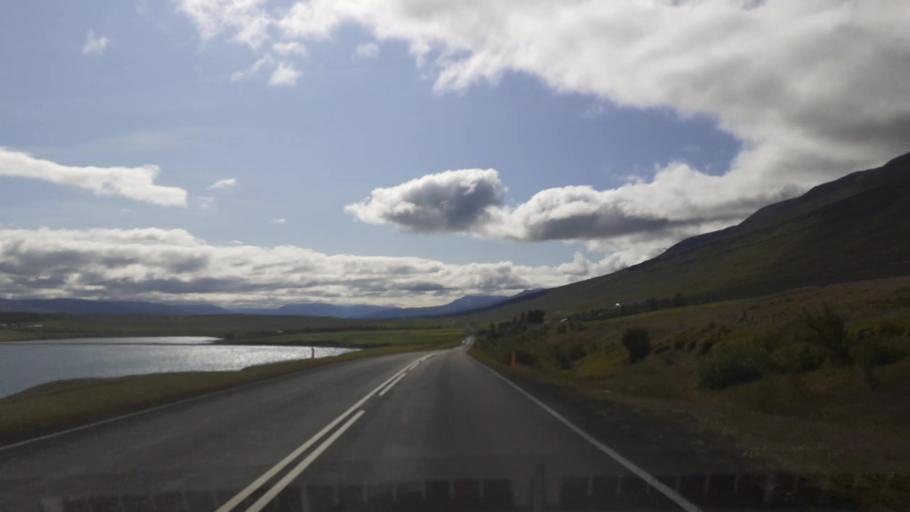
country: IS
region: Northeast
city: Akureyri
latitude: 65.8761
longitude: -18.2648
